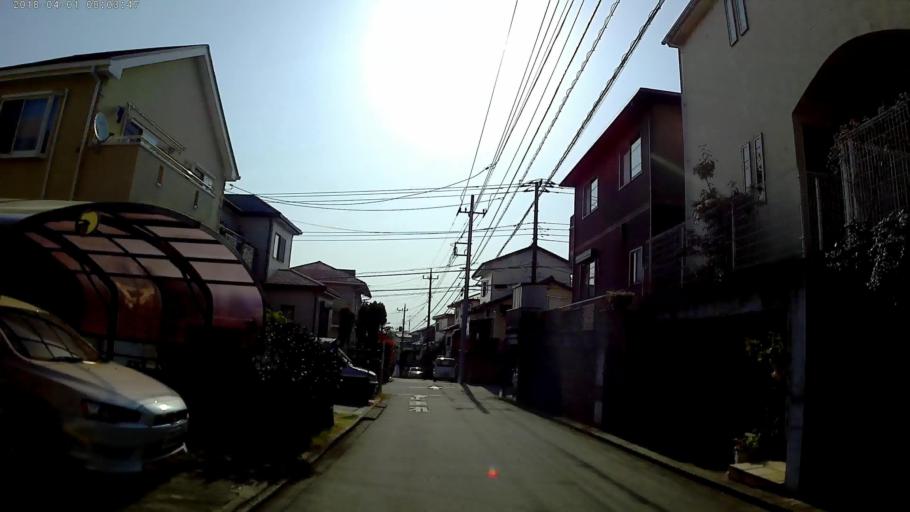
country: JP
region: Kanagawa
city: Atsugi
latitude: 35.4340
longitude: 139.4106
